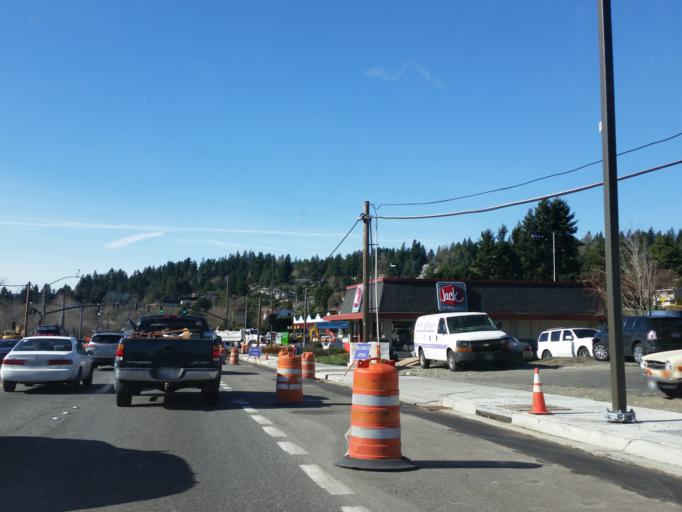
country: US
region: Washington
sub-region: King County
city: Kenmore
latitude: 47.7585
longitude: -122.2609
